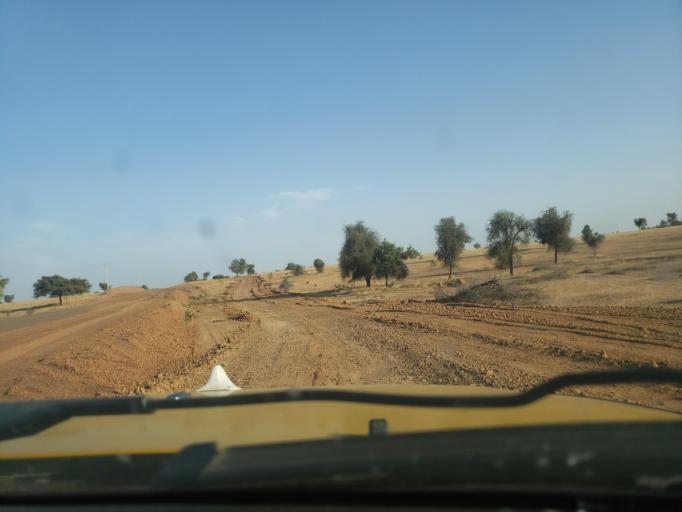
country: SN
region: Louga
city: Dara
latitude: 15.4278
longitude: -15.7437
